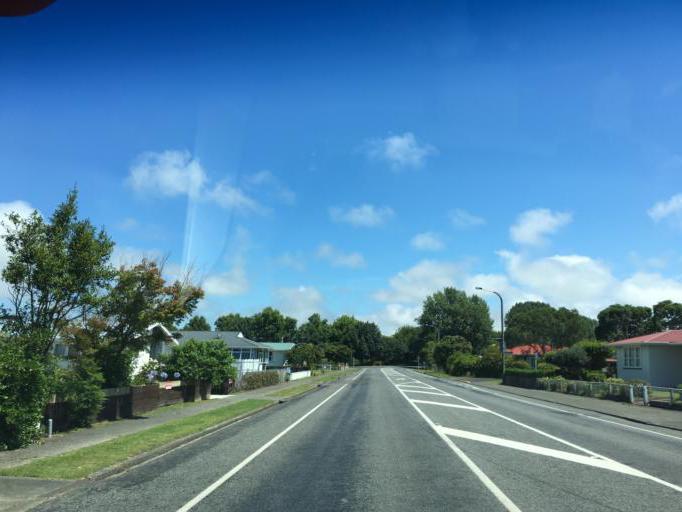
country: NZ
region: Hawke's Bay
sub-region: Wairoa District
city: Wairoa
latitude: -39.0368
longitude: 177.4160
